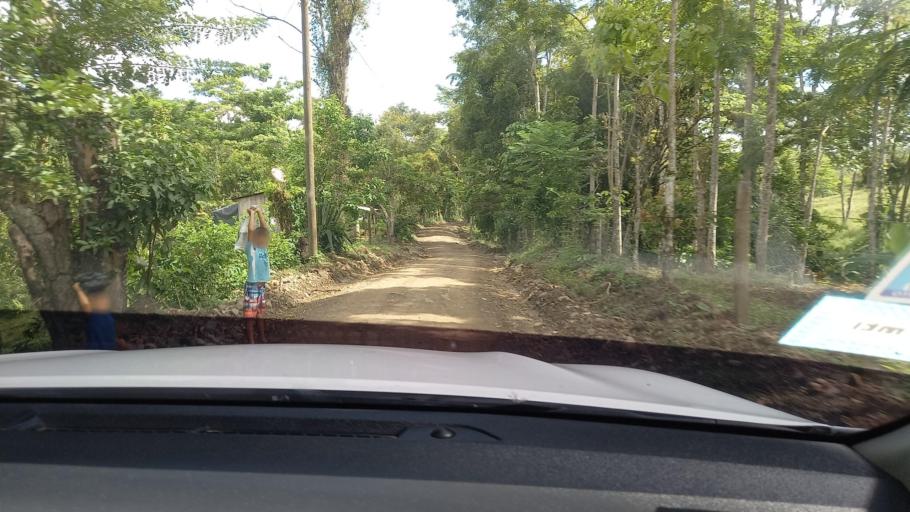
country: NI
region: Jinotega
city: San Jose de Bocay
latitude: 13.3801
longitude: -85.6850
